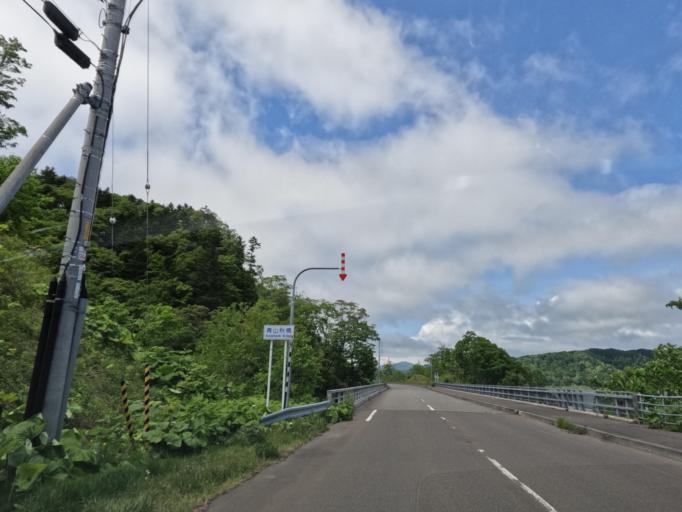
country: JP
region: Hokkaido
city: Tobetsu
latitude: 43.3349
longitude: 141.5677
